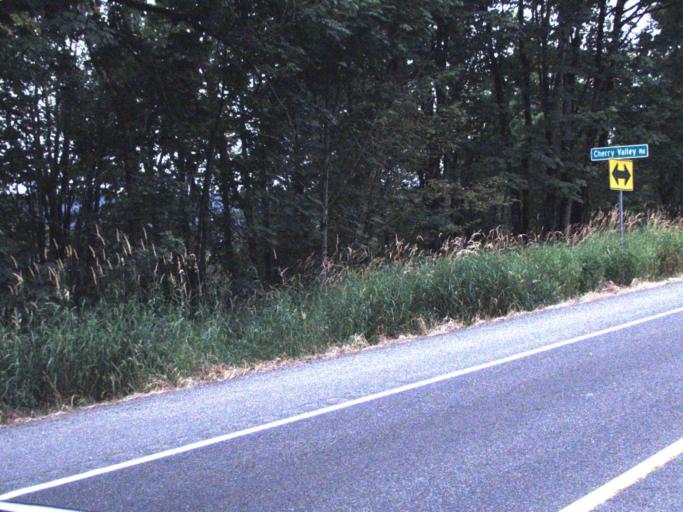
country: US
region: Washington
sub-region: King County
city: Duvall
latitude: 47.7826
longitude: -121.9673
